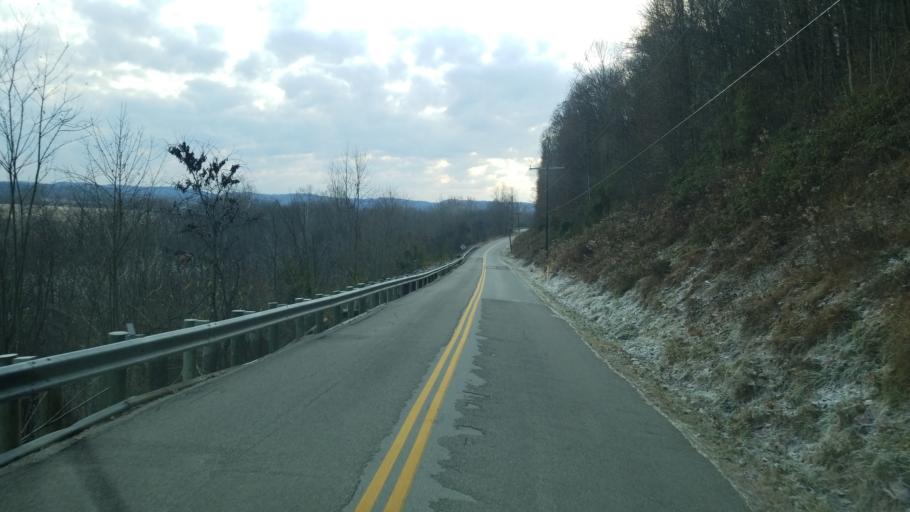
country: US
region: Ohio
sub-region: Pike County
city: Waverly
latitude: 39.2157
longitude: -82.8716
